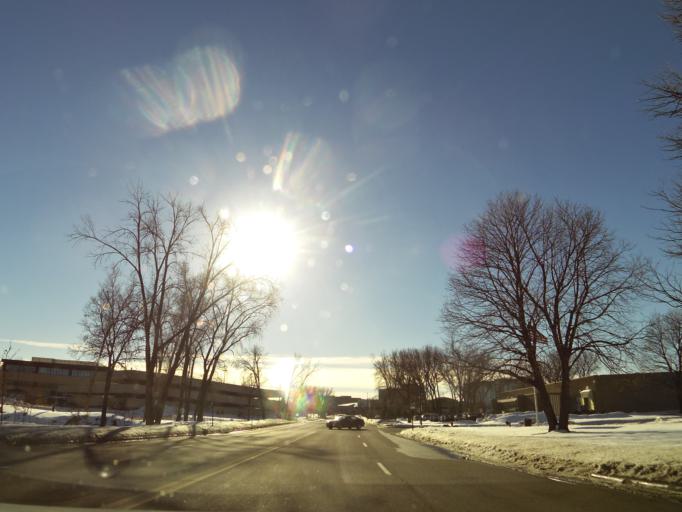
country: US
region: Minnesota
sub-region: Hennepin County
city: Saint Louis Park
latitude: 44.9407
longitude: -93.3396
